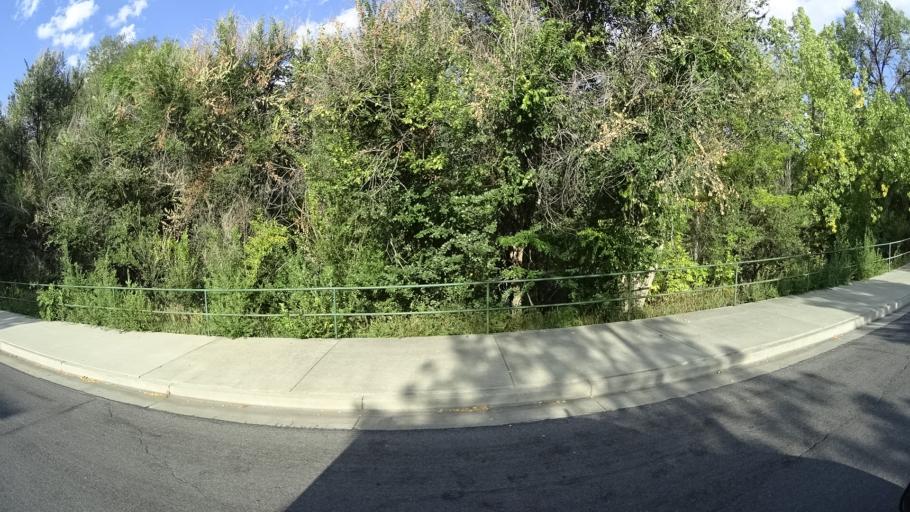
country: US
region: Colorado
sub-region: El Paso County
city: Colorado Springs
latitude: 38.8249
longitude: -104.8166
